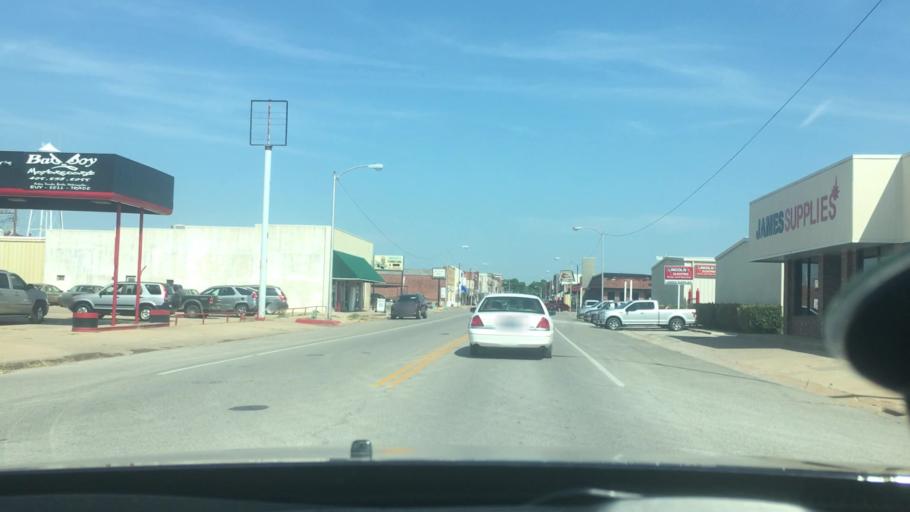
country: US
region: Oklahoma
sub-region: Garvin County
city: Pauls Valley
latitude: 34.7382
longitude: -97.2169
